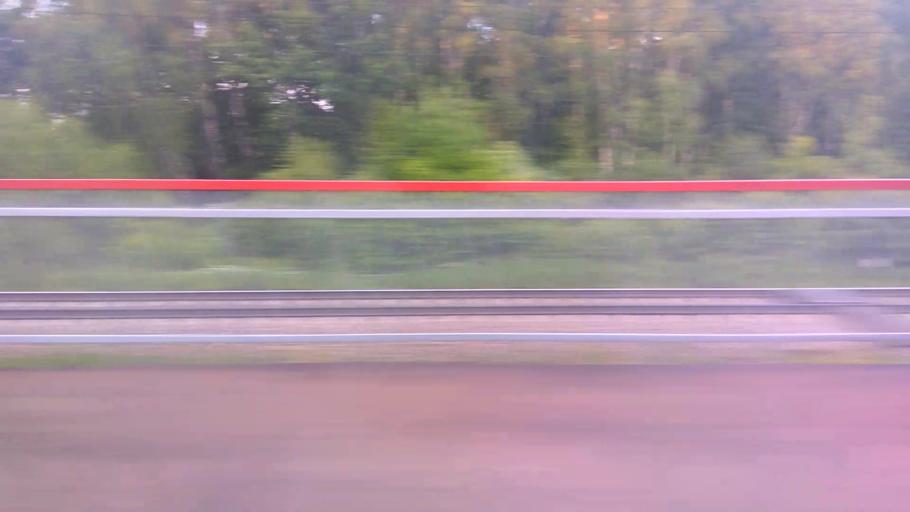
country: RU
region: Moskovskaya
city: Il'inskoye
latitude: 55.2022
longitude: 37.9221
